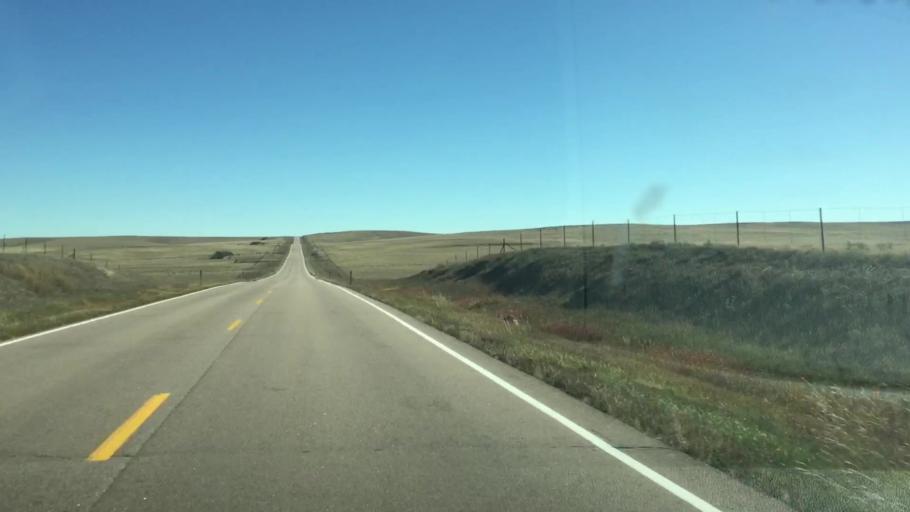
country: US
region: Colorado
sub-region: Lincoln County
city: Limon
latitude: 39.2793
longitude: -103.9945
